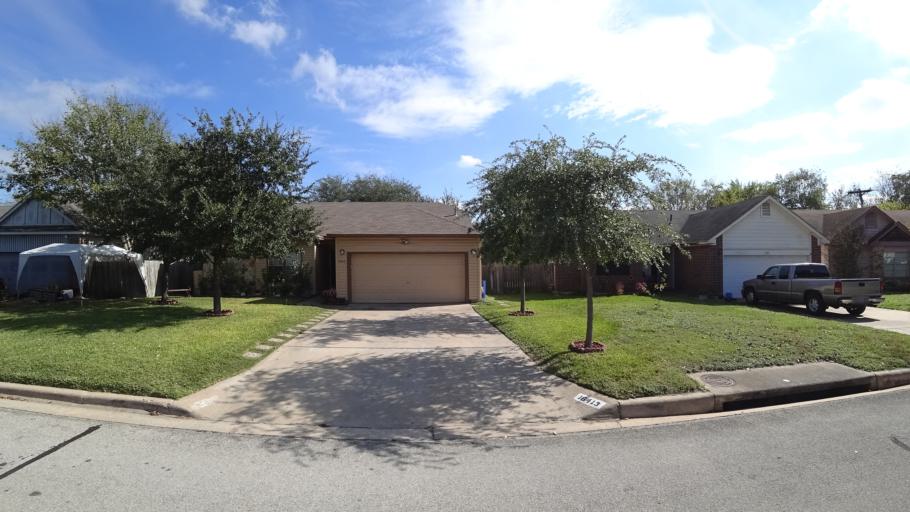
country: US
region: Texas
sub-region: Travis County
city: Windemere
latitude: 30.4540
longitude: -97.6431
